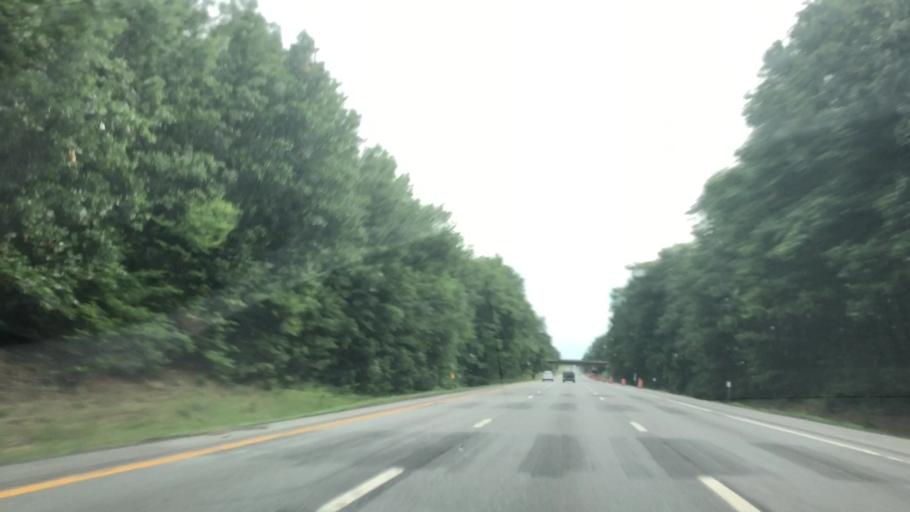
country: US
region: New York
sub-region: Saratoga County
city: Saratoga Springs
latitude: 43.1282
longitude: -73.7379
